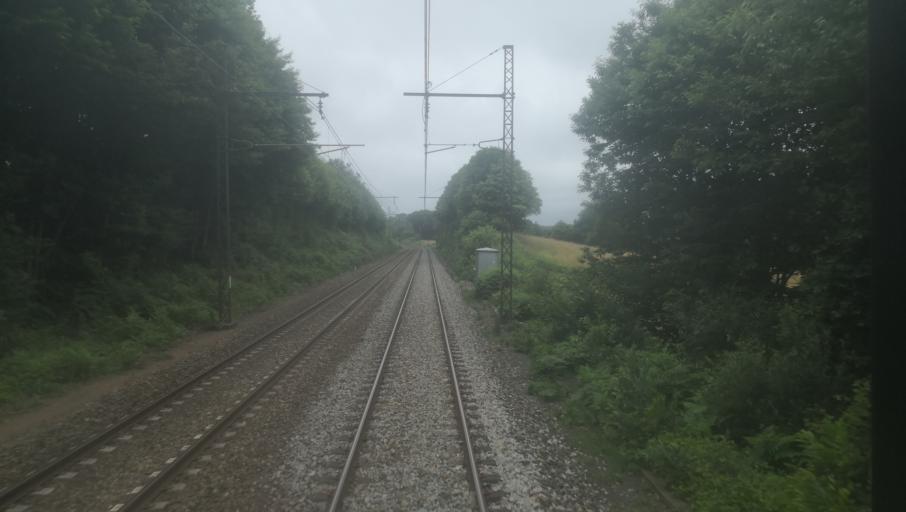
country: FR
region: Limousin
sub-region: Departement de la Creuse
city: La Souterraine
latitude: 46.2685
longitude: 1.4742
